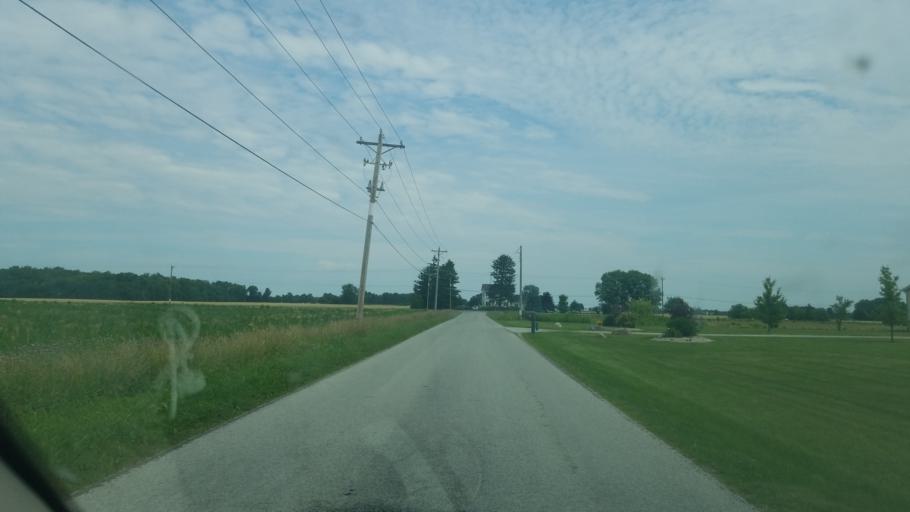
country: US
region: Ohio
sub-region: Seneca County
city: Fostoria
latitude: 41.0711
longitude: -83.4634
